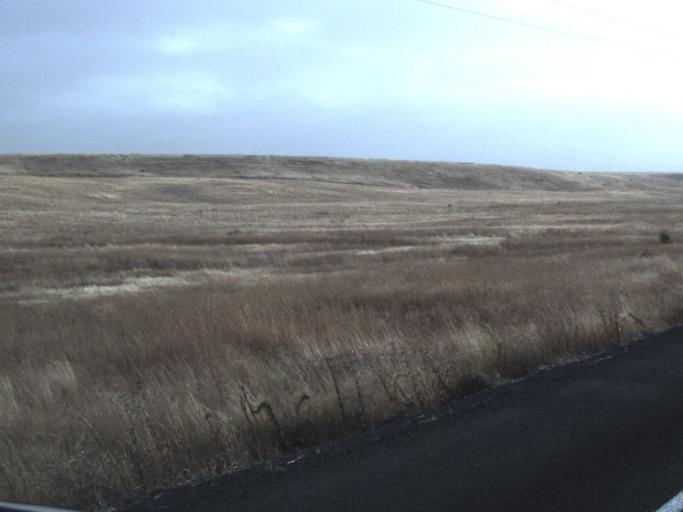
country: US
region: Washington
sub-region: Lincoln County
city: Davenport
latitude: 47.5386
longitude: -118.1961
